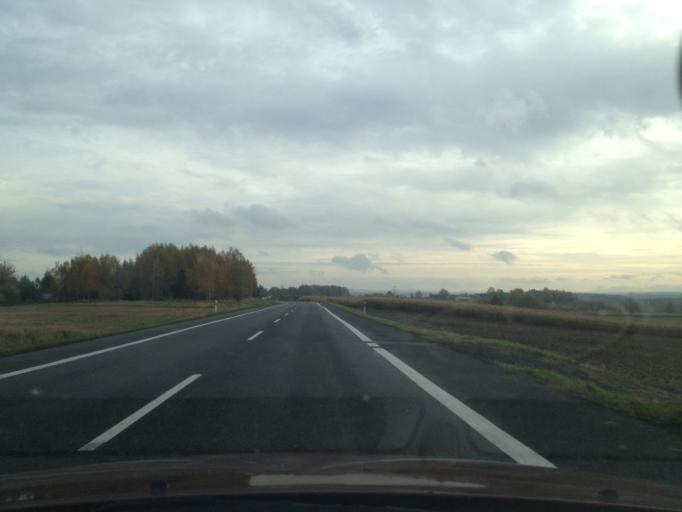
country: PL
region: Lower Silesian Voivodeship
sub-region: Powiat lubanski
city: Pisarzowice
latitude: 51.1426
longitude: 15.2243
